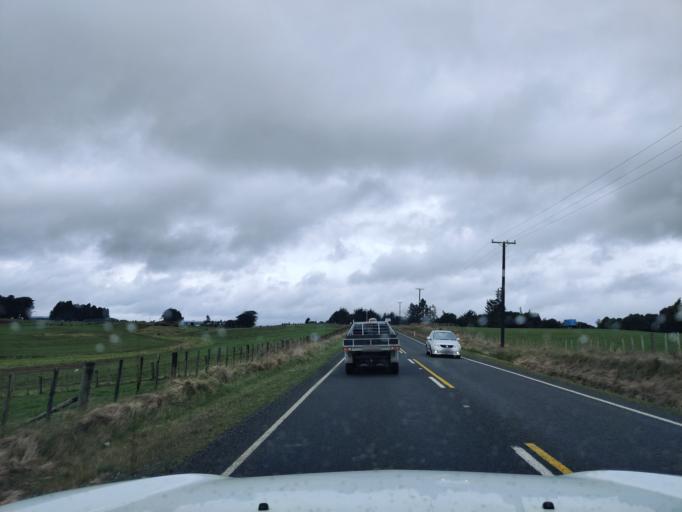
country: NZ
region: Manawatu-Wanganui
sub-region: Ruapehu District
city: Waiouru
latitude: -39.3642
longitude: 175.3409
